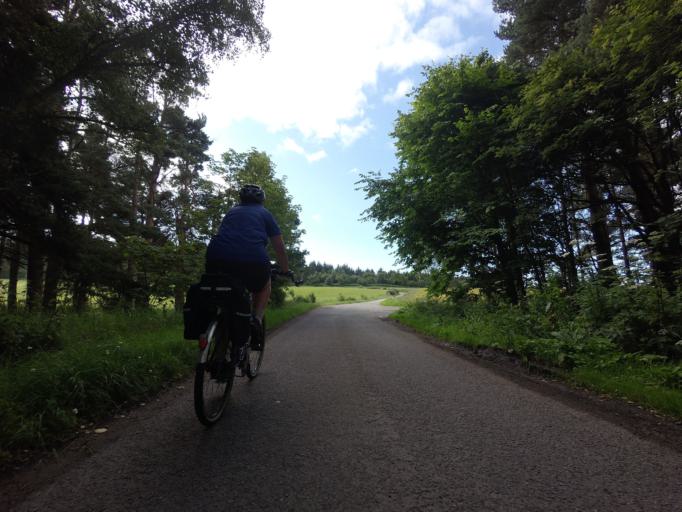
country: GB
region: Scotland
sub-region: Highland
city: Nairn
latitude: 57.5608
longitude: -3.8673
